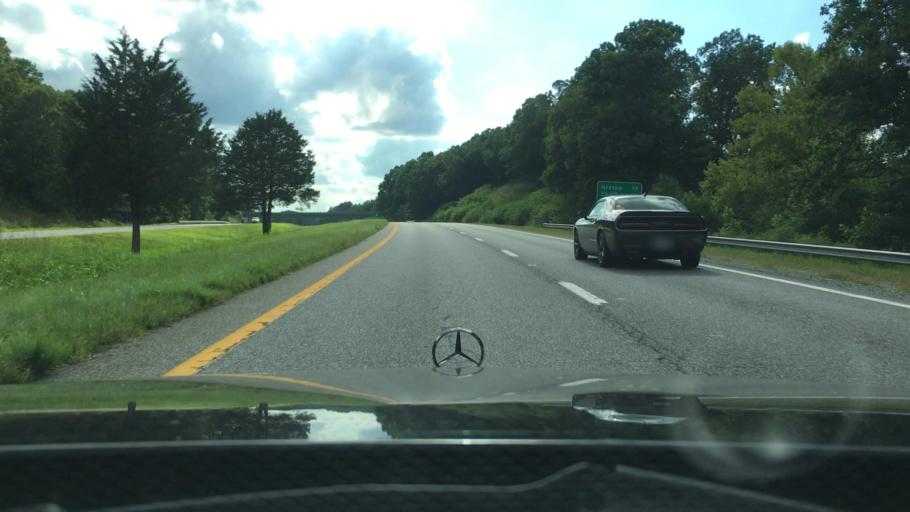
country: US
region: Virginia
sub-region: Campbell County
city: Altavista
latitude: 37.1395
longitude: -79.2632
